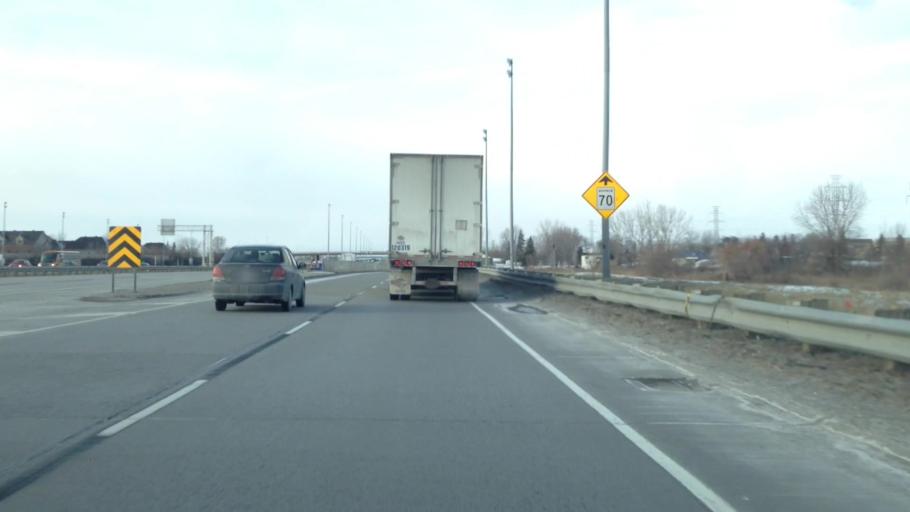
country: CA
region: Quebec
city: Dollard-Des Ormeaux
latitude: 45.5185
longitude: -73.7711
